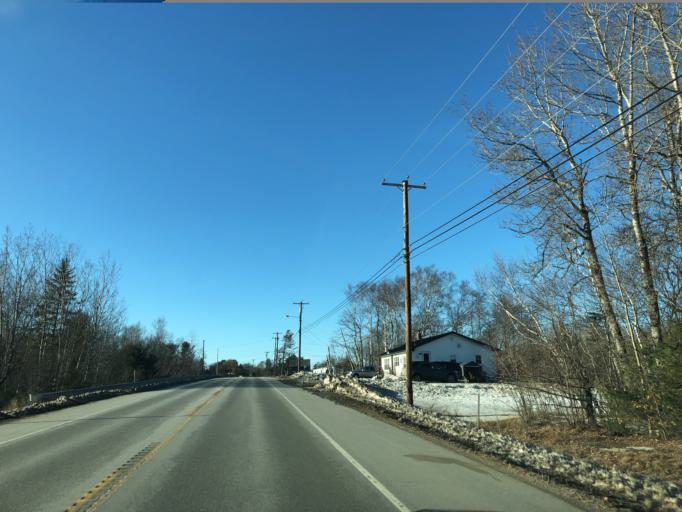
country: US
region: Maine
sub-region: Penobscot County
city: Kenduskeag
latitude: 44.9304
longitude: -68.9361
